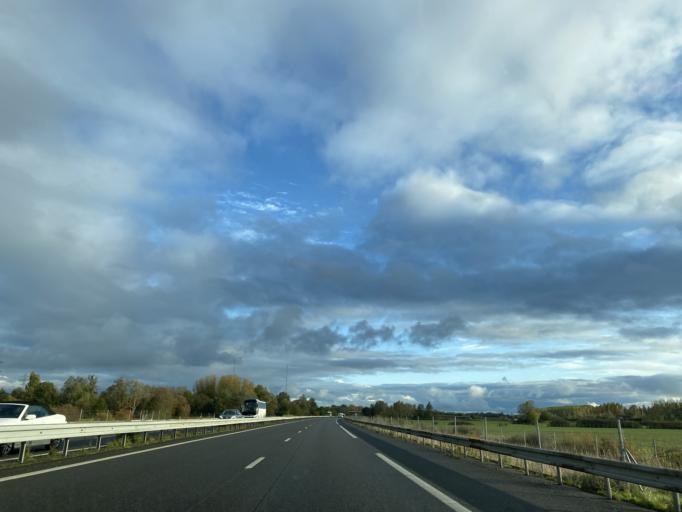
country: FR
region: Centre
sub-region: Departement du Cher
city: Vignoux-sur-Barangeon
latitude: 47.1914
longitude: 2.1608
